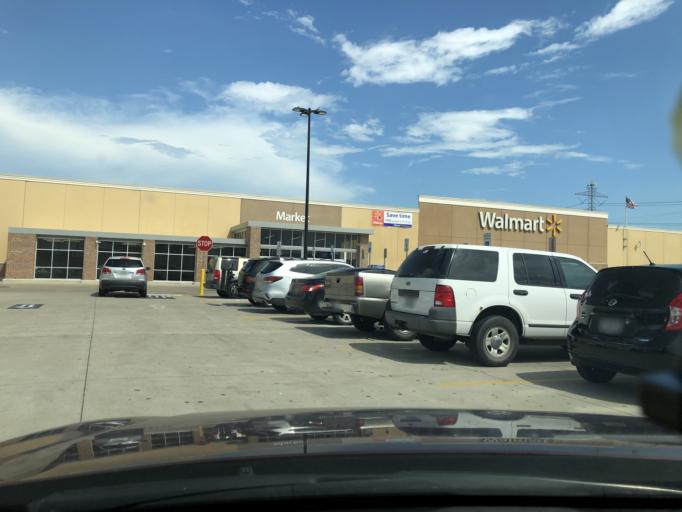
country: US
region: Texas
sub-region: Harris County
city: Bellaire
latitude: 29.7235
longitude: -95.4660
